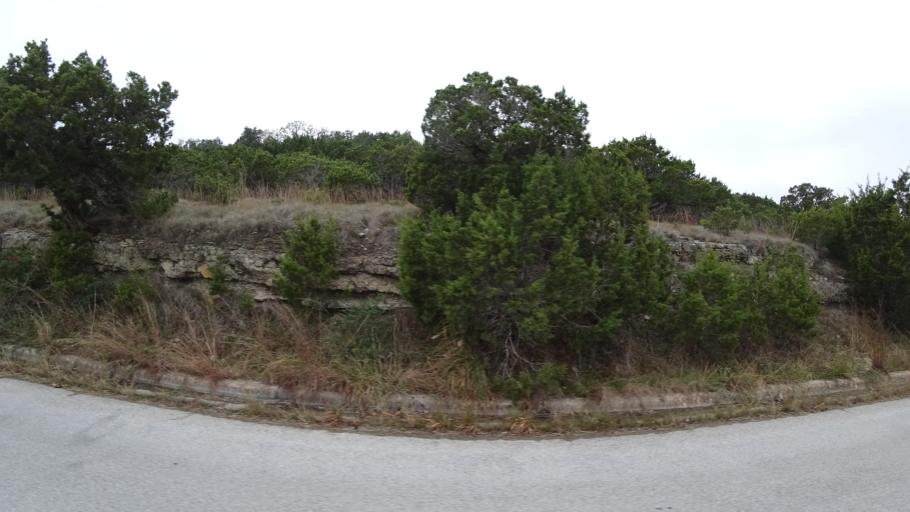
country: US
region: Texas
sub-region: Travis County
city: Barton Creek
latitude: 30.2232
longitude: -97.9046
